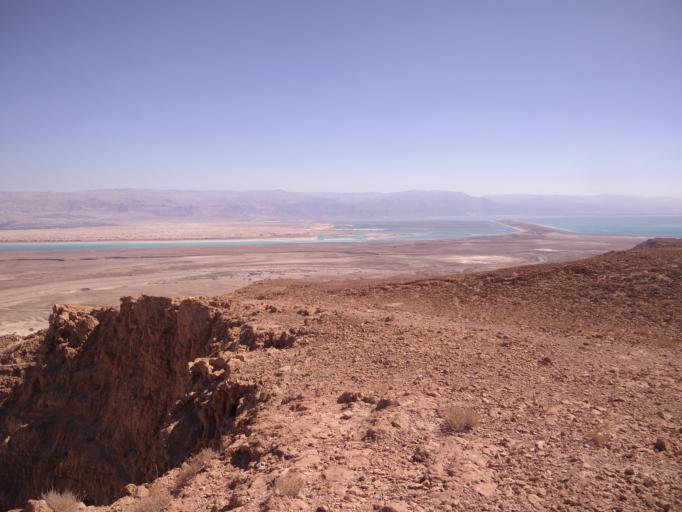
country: IL
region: Southern District
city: `En Boqeq
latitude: 31.3097
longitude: 35.3569
